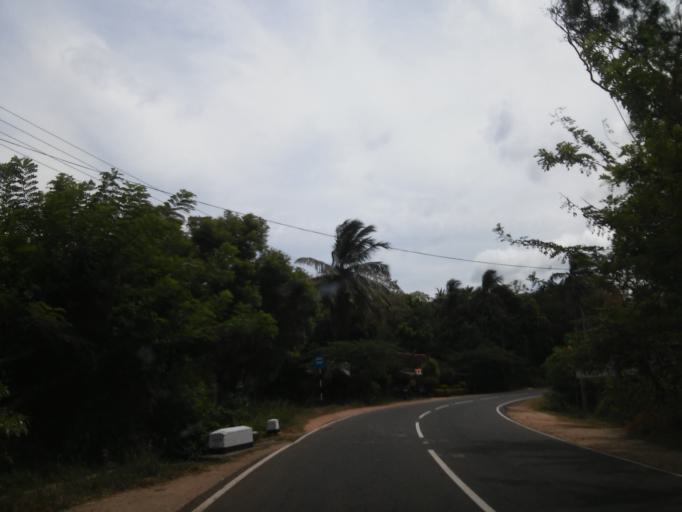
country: LK
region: Eastern Province
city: Trincomalee
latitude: 8.3516
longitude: 80.9832
